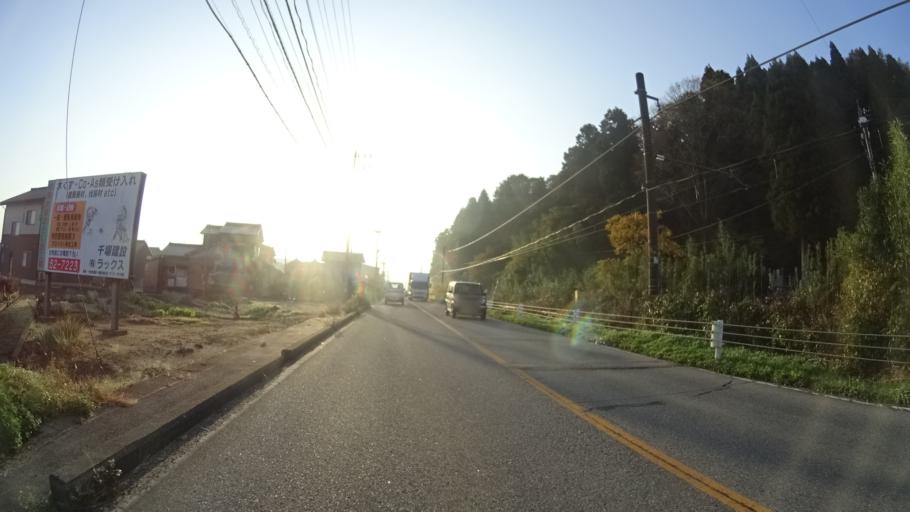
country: JP
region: Ishikawa
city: Nanao
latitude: 37.0673
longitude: 136.9356
